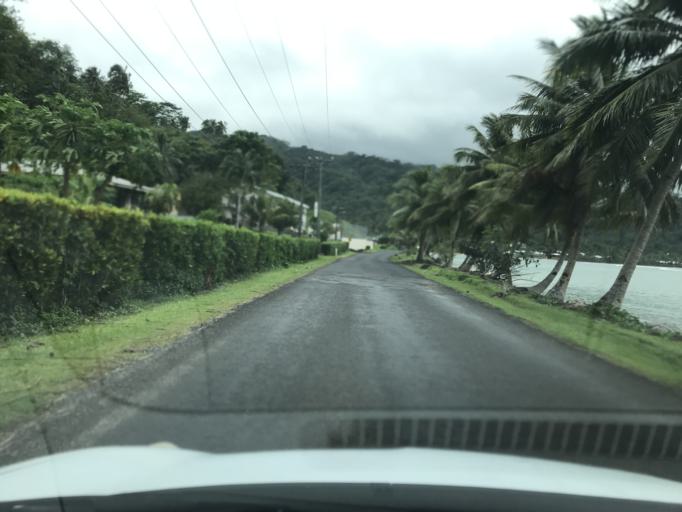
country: WS
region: Atua
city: Lufilufi
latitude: -13.8826
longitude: -171.6172
